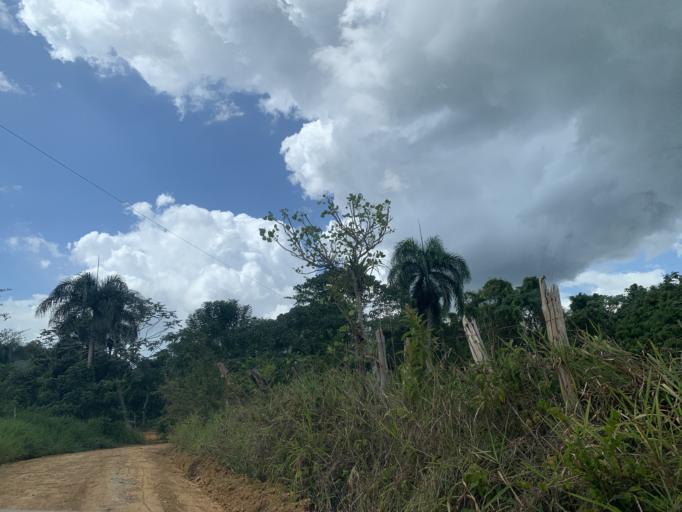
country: DO
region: Monte Plata
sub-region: Yamasa
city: Yamasa
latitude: 18.7815
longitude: -70.0279
